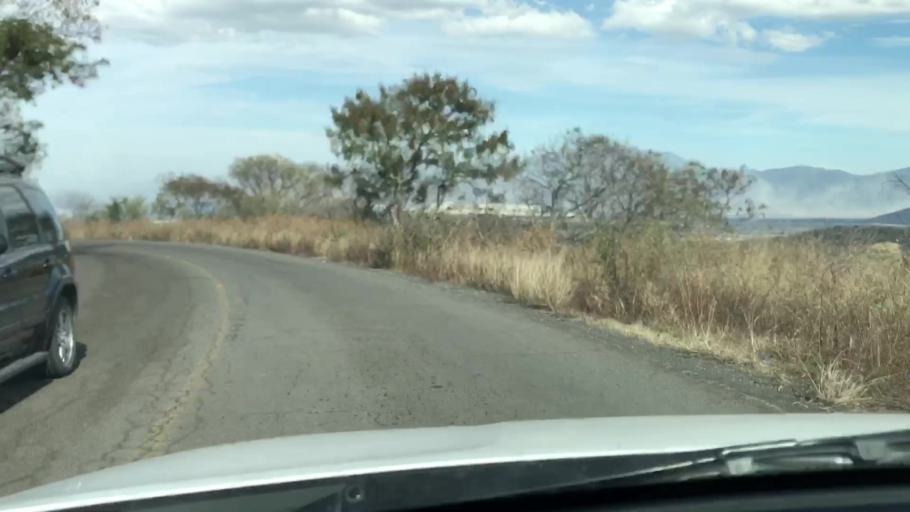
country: MX
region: Jalisco
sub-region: Zacoalco de Torres
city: Barranca de Otates (Barranca de Otatan)
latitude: 20.2455
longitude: -103.6672
